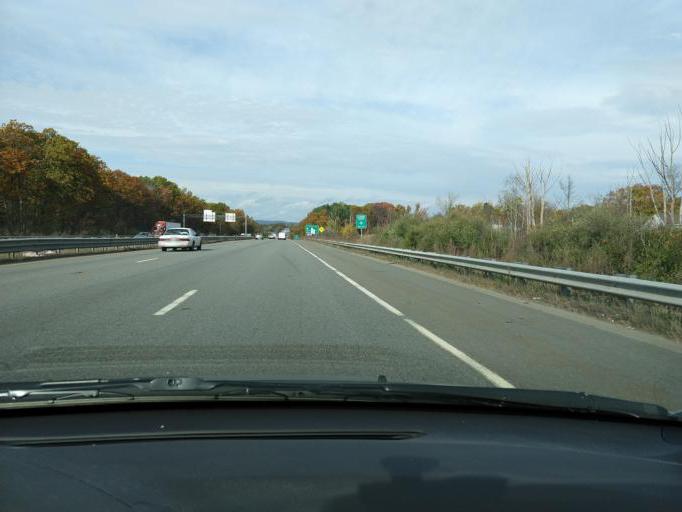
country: US
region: Massachusetts
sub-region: Worcester County
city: Leominster
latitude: 42.5308
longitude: -71.7357
